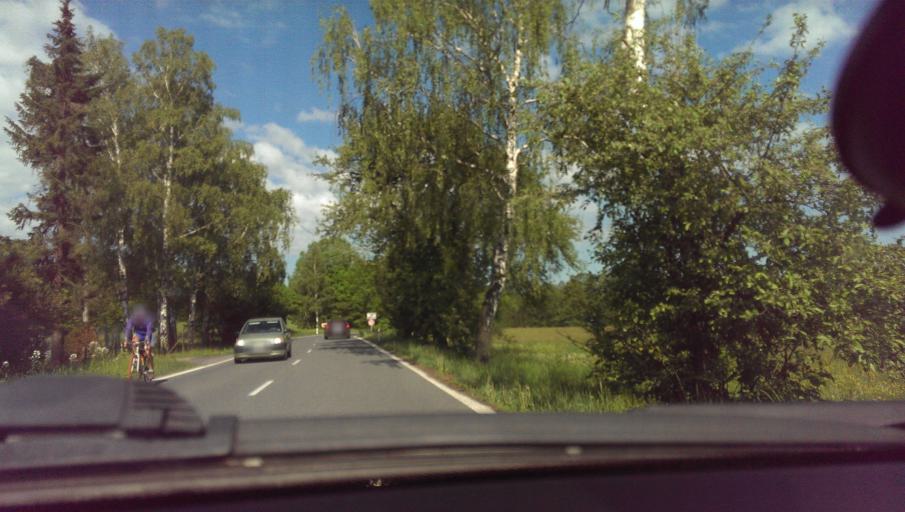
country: CZ
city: Kuncice pod Ondrejnikem
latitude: 49.5444
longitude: 18.2622
